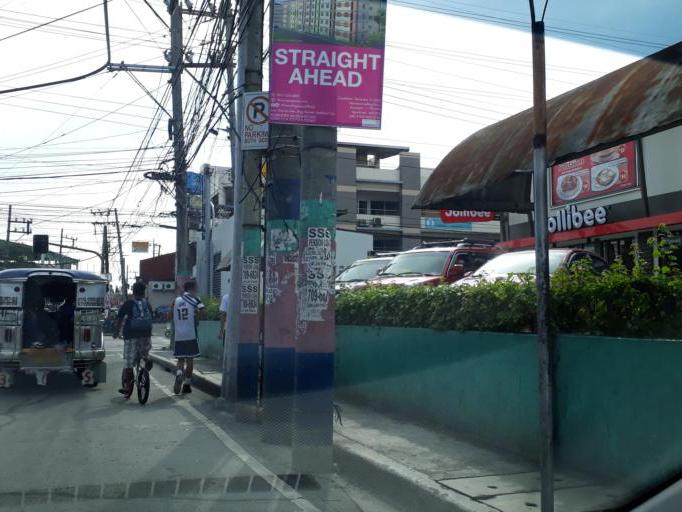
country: PH
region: Metro Manila
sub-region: Caloocan City
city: Niugan
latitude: 14.6680
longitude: 120.9660
